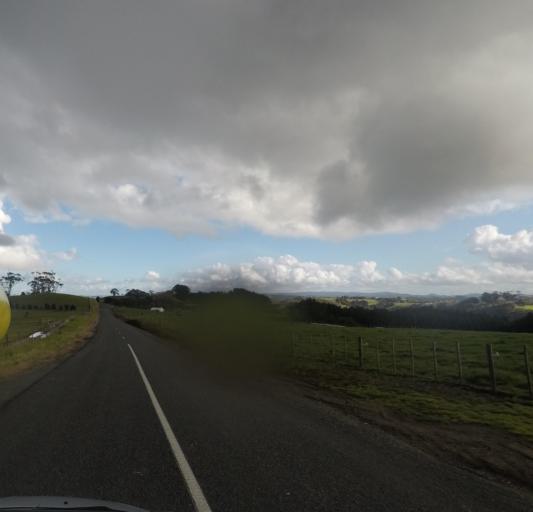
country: NZ
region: Auckland
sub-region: Auckland
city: Warkworth
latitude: -36.3686
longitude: 174.7662
